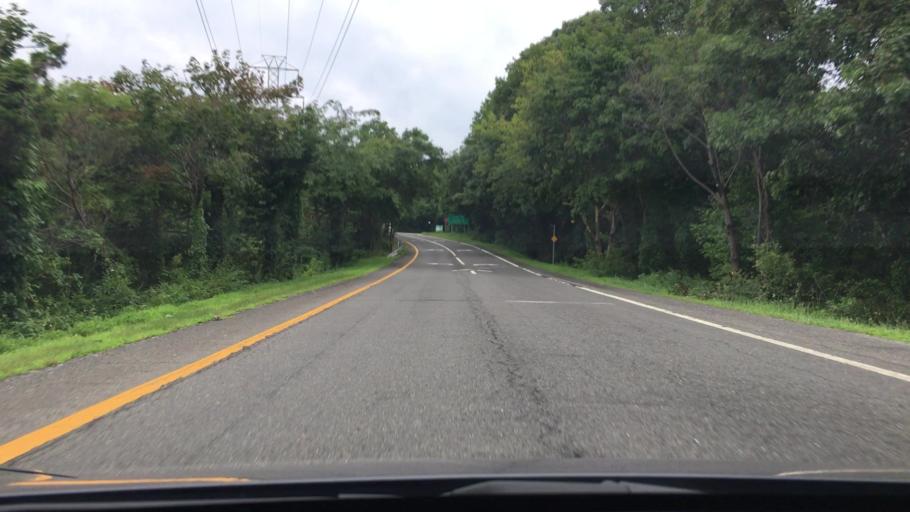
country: US
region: New York
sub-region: Nassau County
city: Bethpage
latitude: 40.7447
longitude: -73.4744
